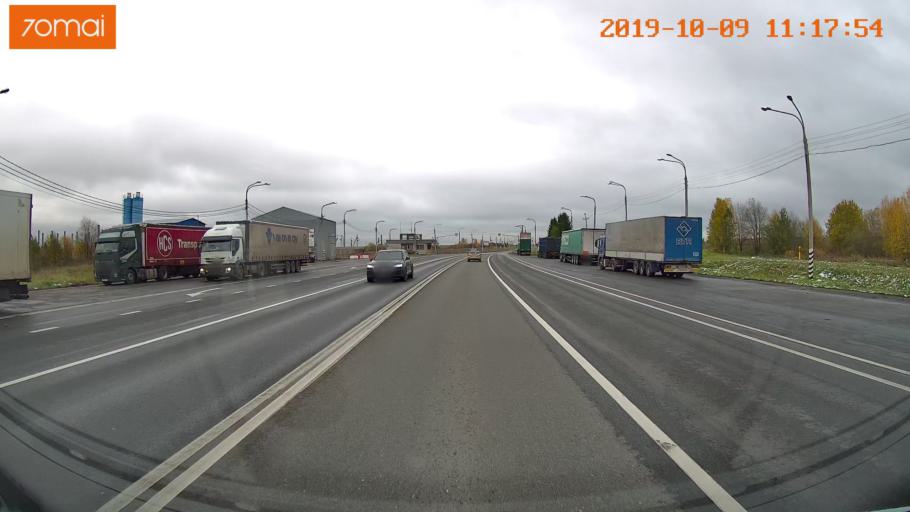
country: RU
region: Vologda
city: Vologda
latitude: 59.1718
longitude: 39.9066
